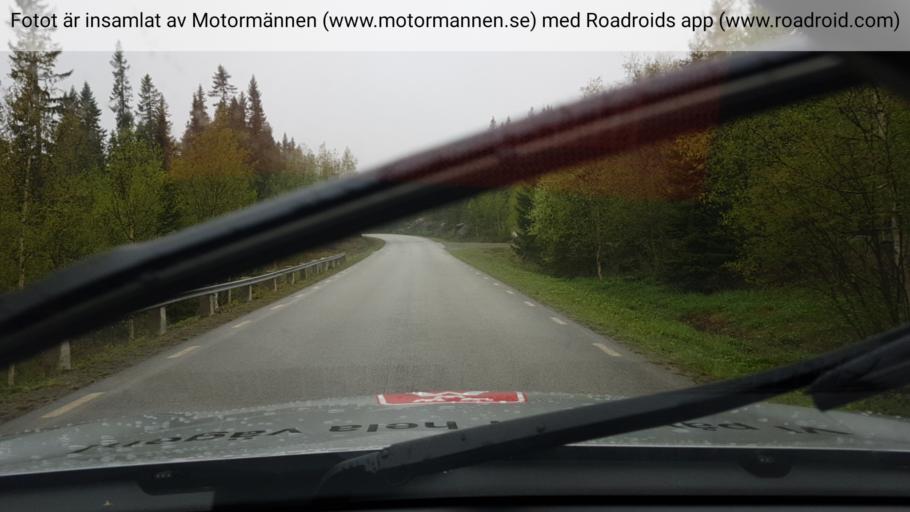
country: SE
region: Jaemtland
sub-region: Bergs Kommun
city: Hoverberg
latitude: 63.0381
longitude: 14.0361
